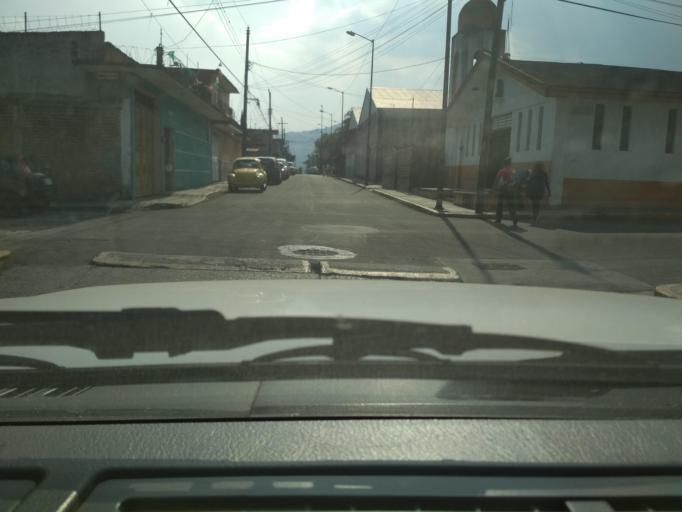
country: MX
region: Veracruz
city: Orizaba
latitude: 18.8693
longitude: -97.0947
